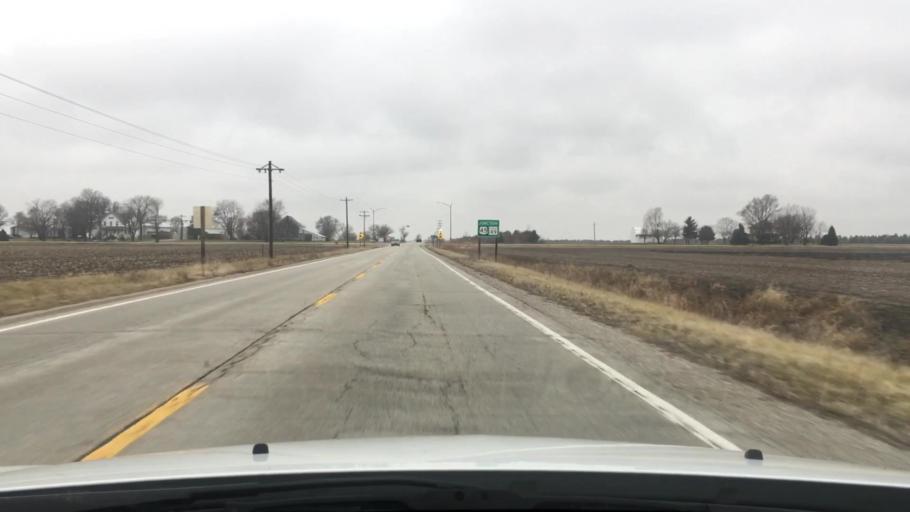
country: US
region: Illinois
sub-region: Iroquois County
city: Clifton
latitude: 40.8872
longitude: -87.8622
